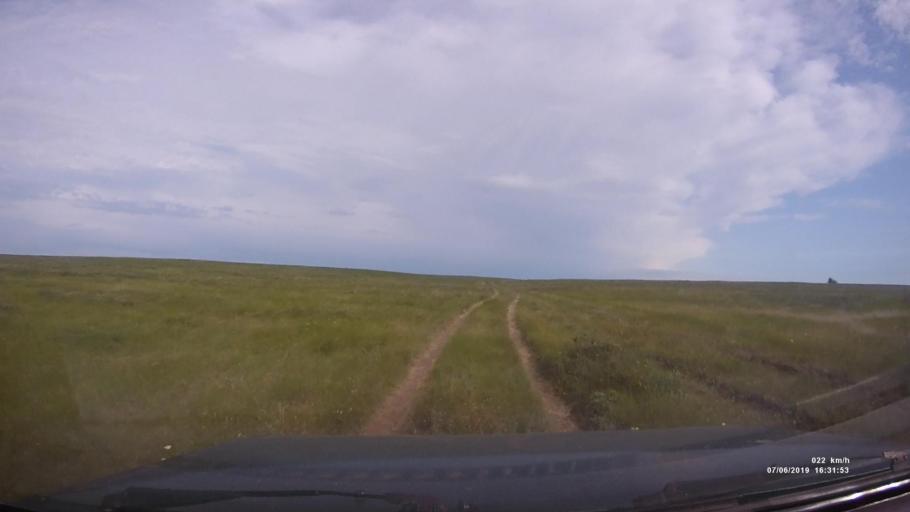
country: RU
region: Rostov
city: Staraya Stanitsa
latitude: 48.2550
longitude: 40.3281
